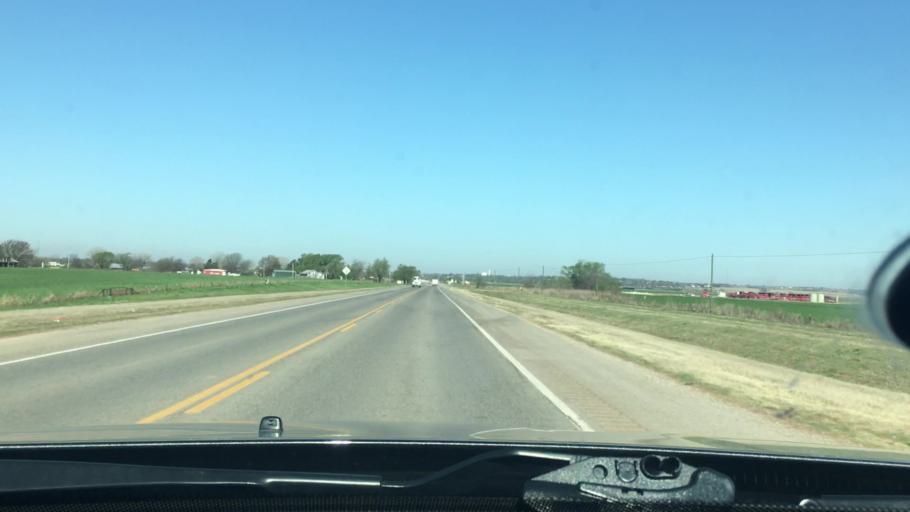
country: US
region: Oklahoma
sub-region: Garvin County
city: Lindsay
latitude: 34.8315
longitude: -97.5751
